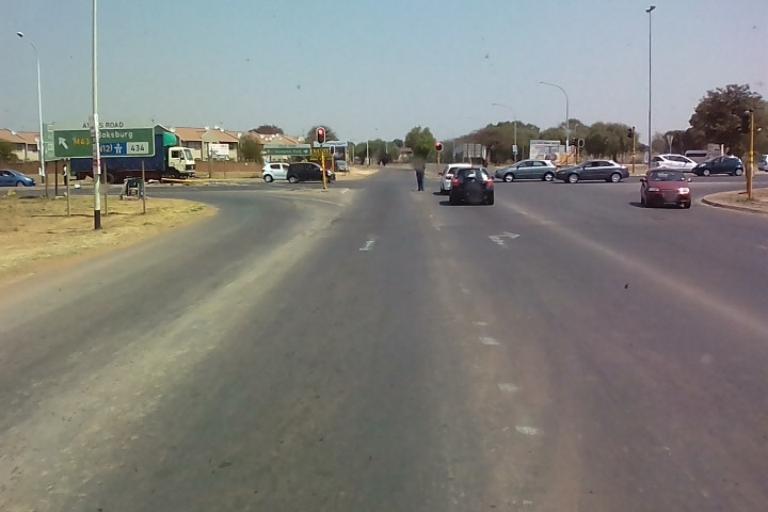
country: ZA
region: Gauteng
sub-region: Ekurhuleni Metropolitan Municipality
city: Benoni
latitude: -26.1596
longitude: 28.2777
